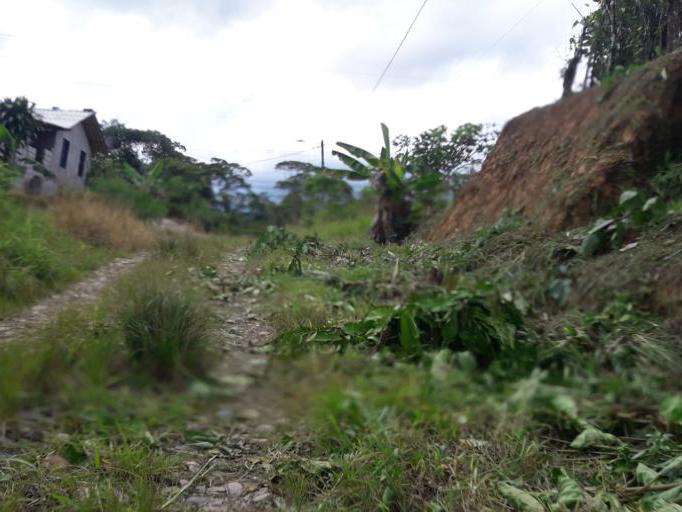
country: EC
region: Napo
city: Tena
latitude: -0.9591
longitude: -77.8163
